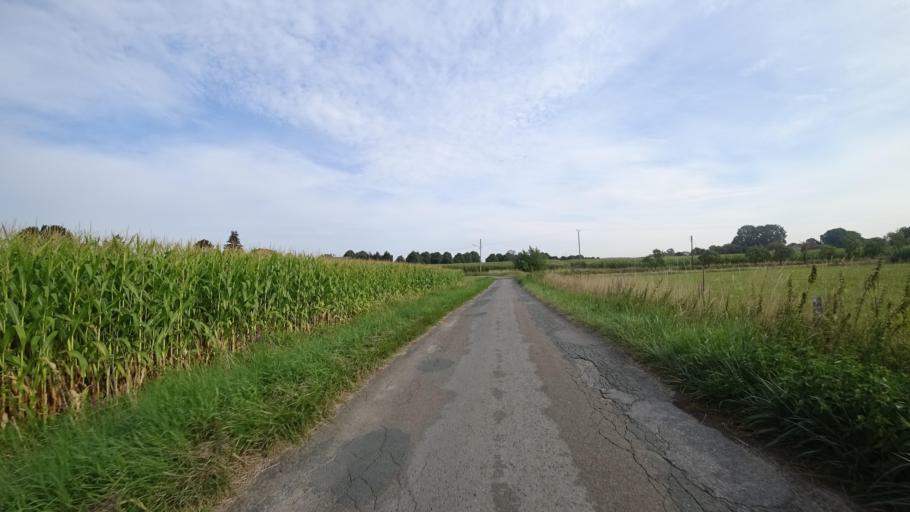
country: DE
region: North Rhine-Westphalia
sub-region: Regierungsbezirk Detmold
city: Steinhagen
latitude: 51.9558
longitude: 8.4486
